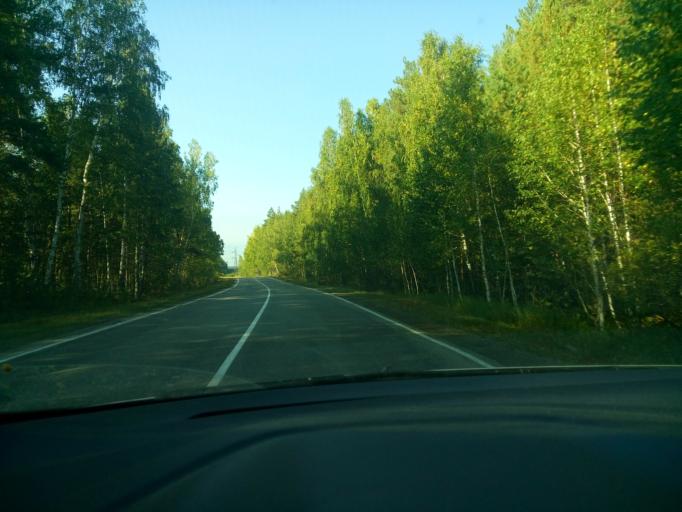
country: RU
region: Chelyabinsk
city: Kasli
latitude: 55.8638
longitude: 60.6864
